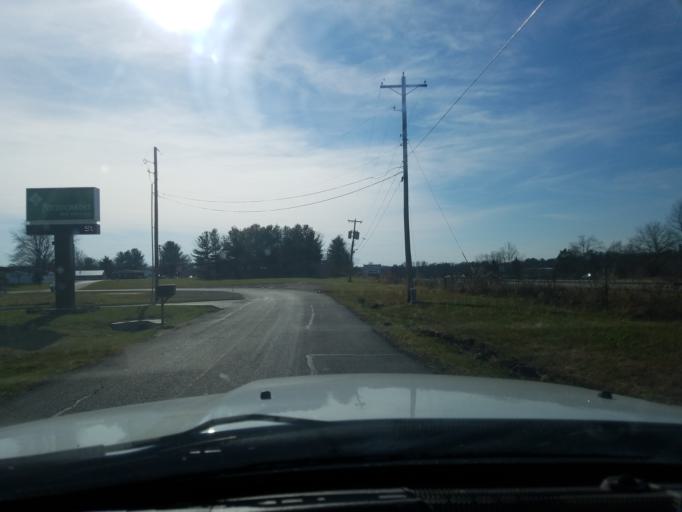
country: US
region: Ohio
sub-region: Athens County
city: Athens
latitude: 39.2343
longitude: -82.1946
